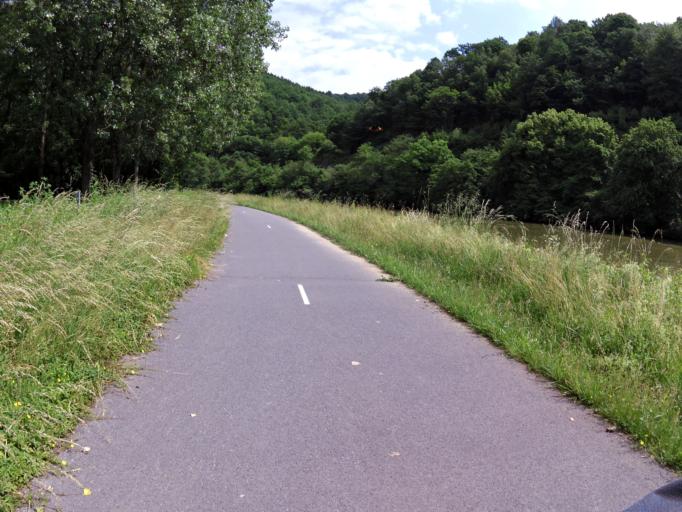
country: FR
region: Champagne-Ardenne
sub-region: Departement des Ardennes
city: Nouzonville
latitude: 49.8319
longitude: 4.7725
